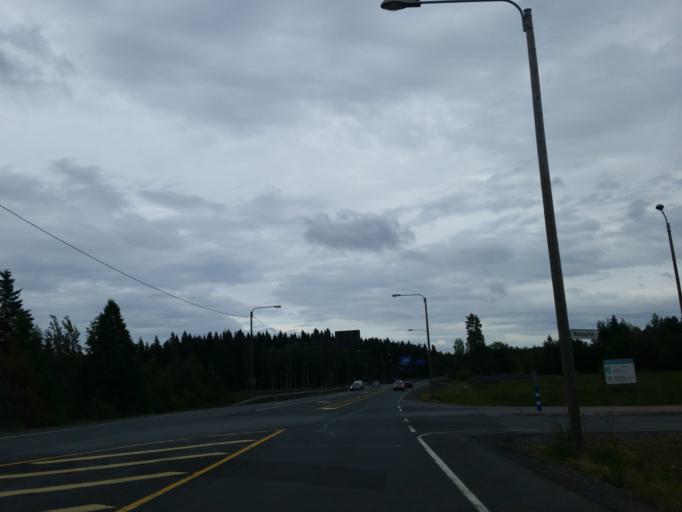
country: FI
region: Northern Savo
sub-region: Kuopio
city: Kuopio
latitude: 62.9858
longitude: 27.7712
